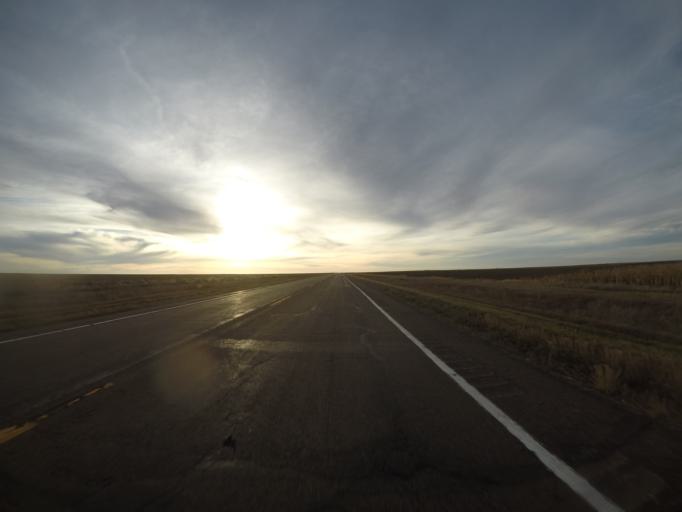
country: US
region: Colorado
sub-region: Washington County
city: Akron
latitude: 39.7274
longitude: -103.1468
